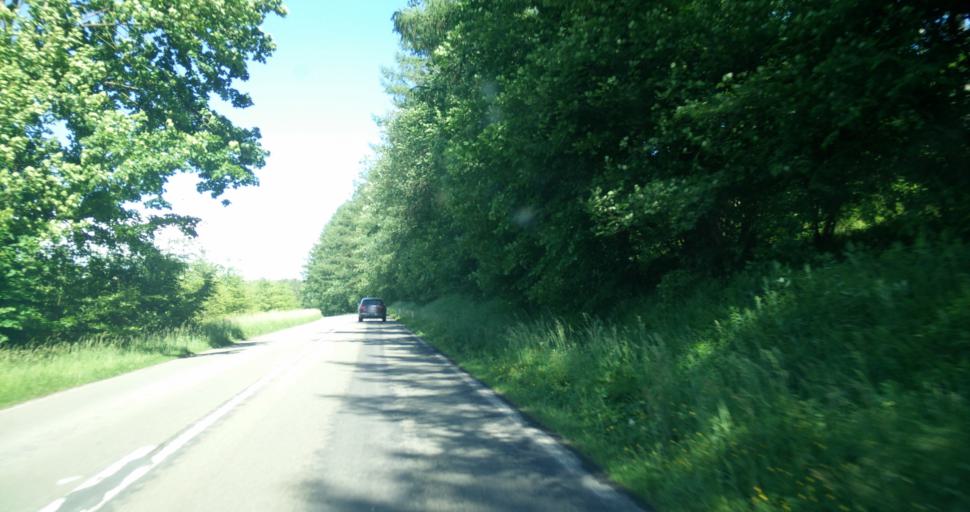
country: BE
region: Wallonia
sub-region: Province du Luxembourg
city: Marche-en-Famenne
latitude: 50.2067
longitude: 5.4068
